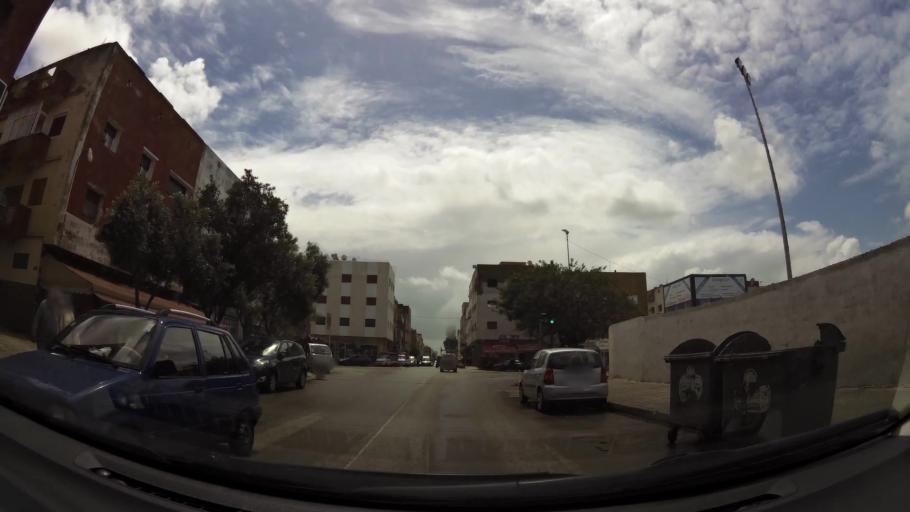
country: MA
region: Grand Casablanca
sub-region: Casablanca
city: Casablanca
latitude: 33.5553
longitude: -7.6785
